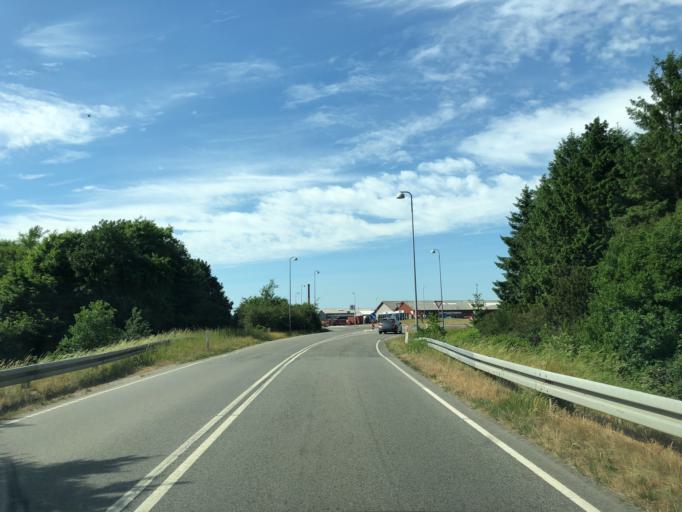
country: DK
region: Central Jutland
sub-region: Ikast-Brande Kommune
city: Brande
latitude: 55.9257
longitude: 9.1583
